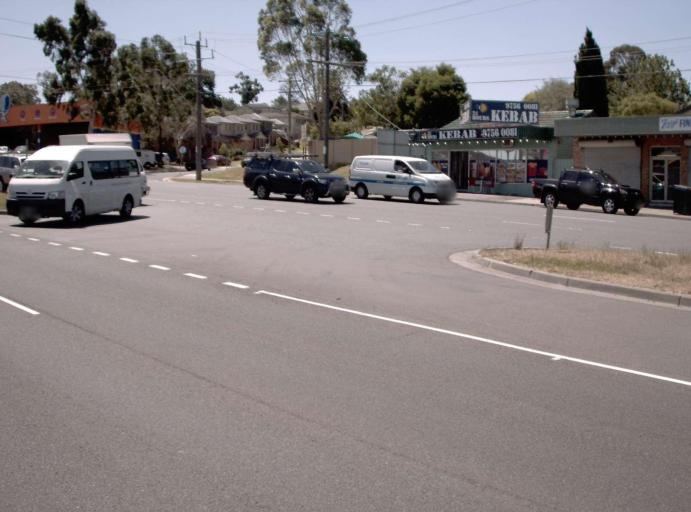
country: AU
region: Victoria
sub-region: Knox
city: Ferntree Gully
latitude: -37.8845
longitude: 145.2821
